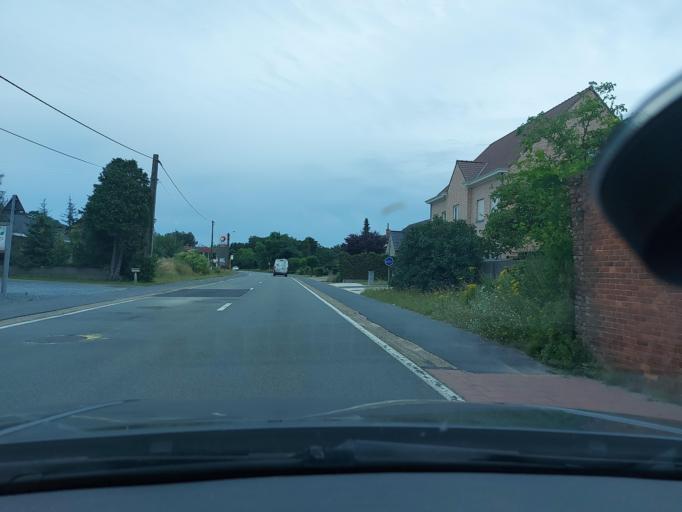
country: BE
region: Flanders
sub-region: Provincie Antwerpen
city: Balen
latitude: 51.1817
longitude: 5.2080
